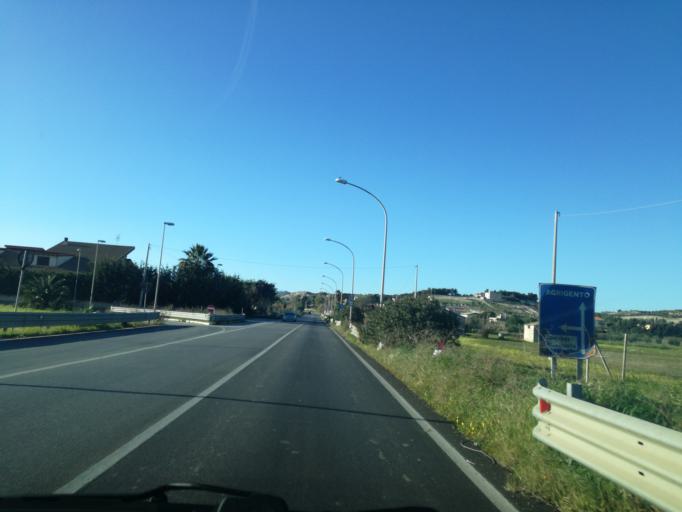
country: IT
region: Sicily
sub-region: Provincia di Caltanissetta
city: Gela
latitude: 37.0979
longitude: 14.1642
